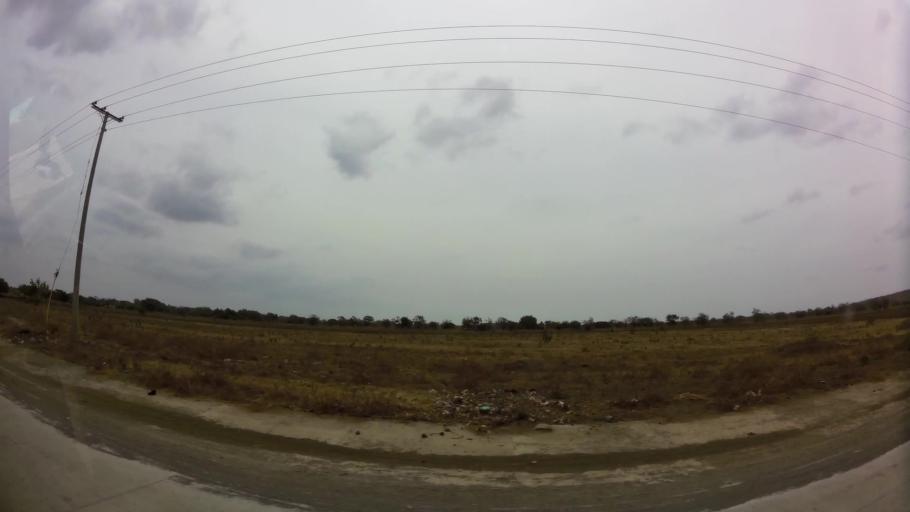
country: NI
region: Managua
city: Managua
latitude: 12.1113
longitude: -86.1734
